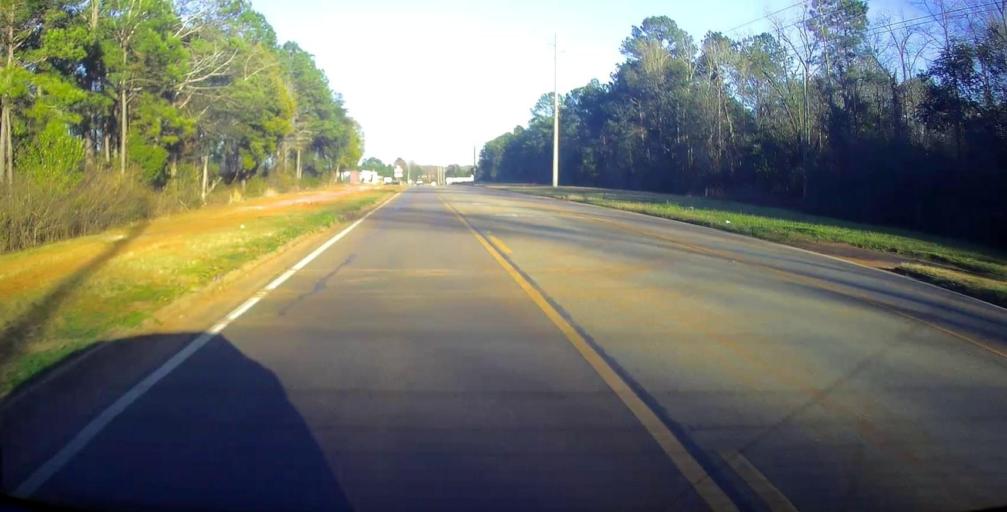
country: US
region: Georgia
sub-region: Dougherty County
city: Albany
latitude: 31.6230
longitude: -84.1814
